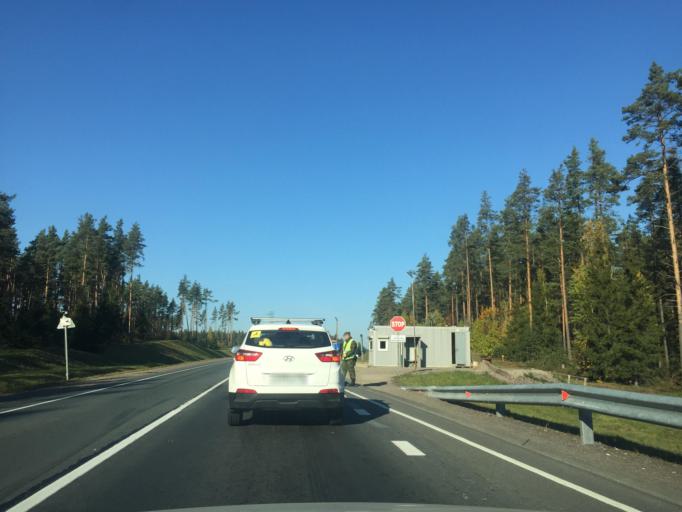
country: RU
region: Leningrad
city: Kuznechnoye
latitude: 61.1667
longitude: 29.8443
